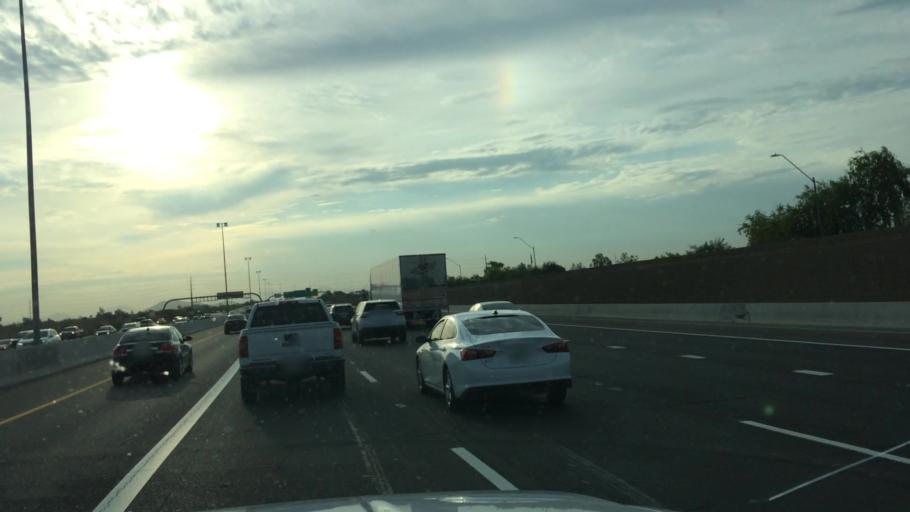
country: US
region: Arizona
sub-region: Maricopa County
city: Peoria
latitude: 33.6690
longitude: -112.1448
